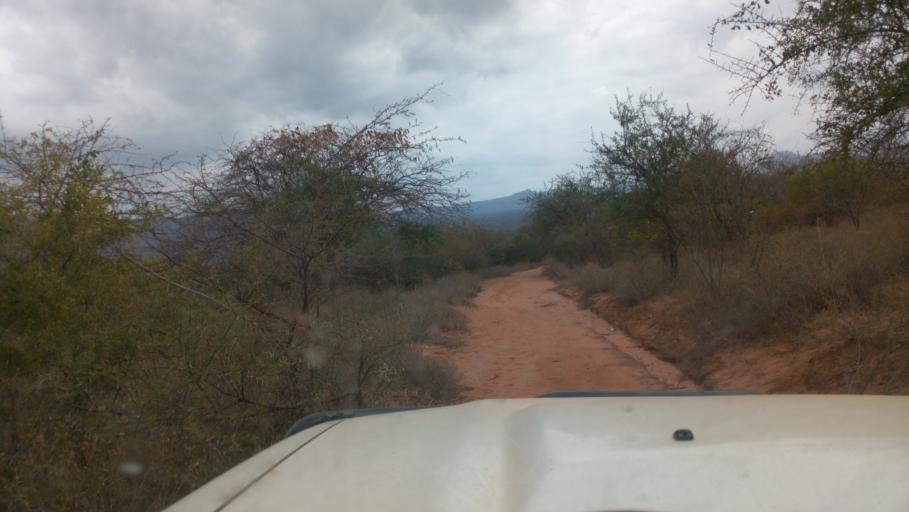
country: KE
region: Kitui
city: Kitui
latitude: -1.8462
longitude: 38.3948
